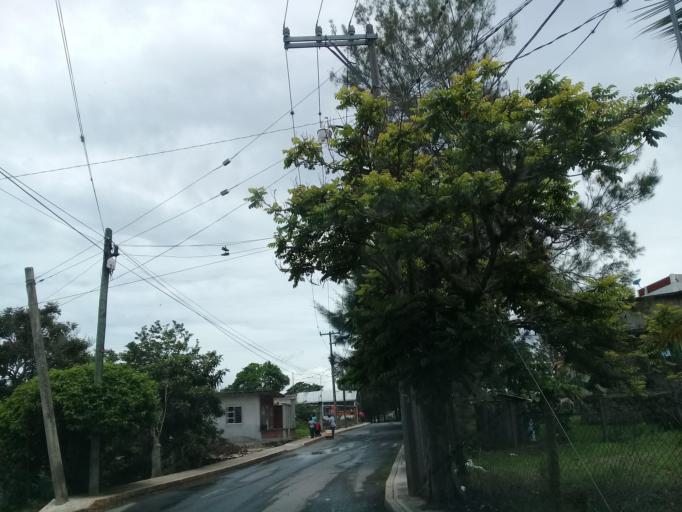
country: MX
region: Veracruz
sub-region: Emiliano Zapata
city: Dos Rios
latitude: 19.4648
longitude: -96.7843
